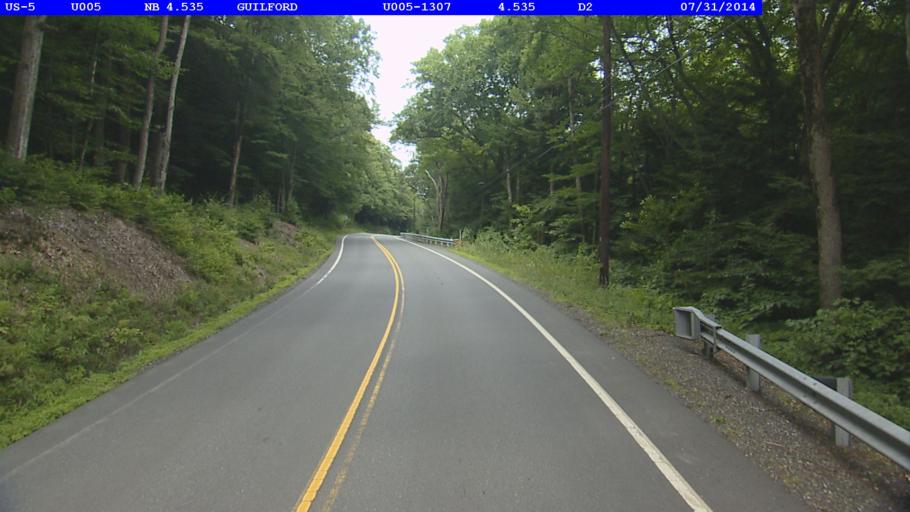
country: US
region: Vermont
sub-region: Windham County
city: Brattleboro
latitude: 42.7929
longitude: -72.5644
